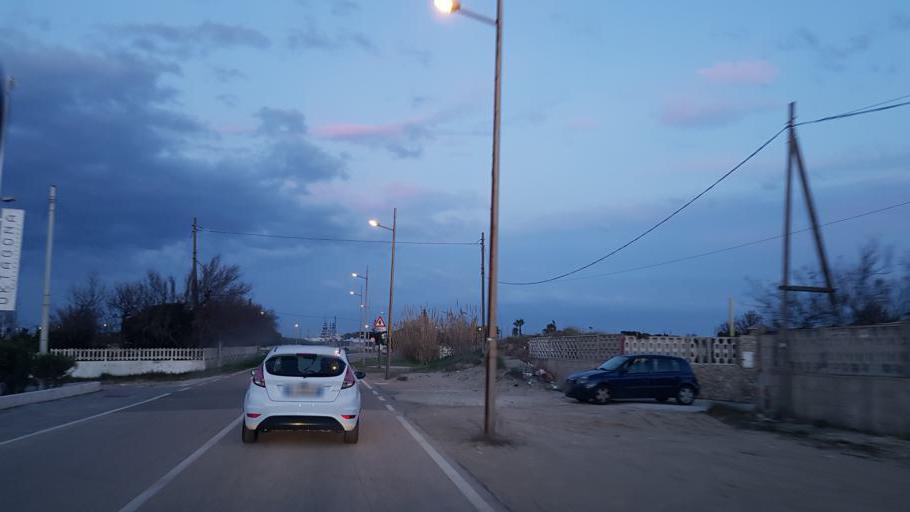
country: IT
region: Apulia
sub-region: Provincia di Brindisi
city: Materdomini
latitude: 40.6791
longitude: 17.9314
